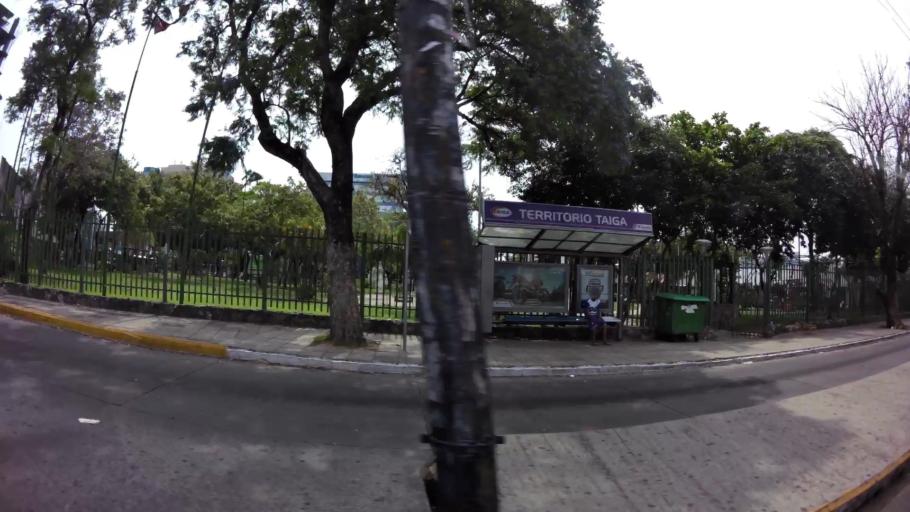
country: PY
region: Asuncion
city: Asuncion
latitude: -25.2949
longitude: -57.5769
